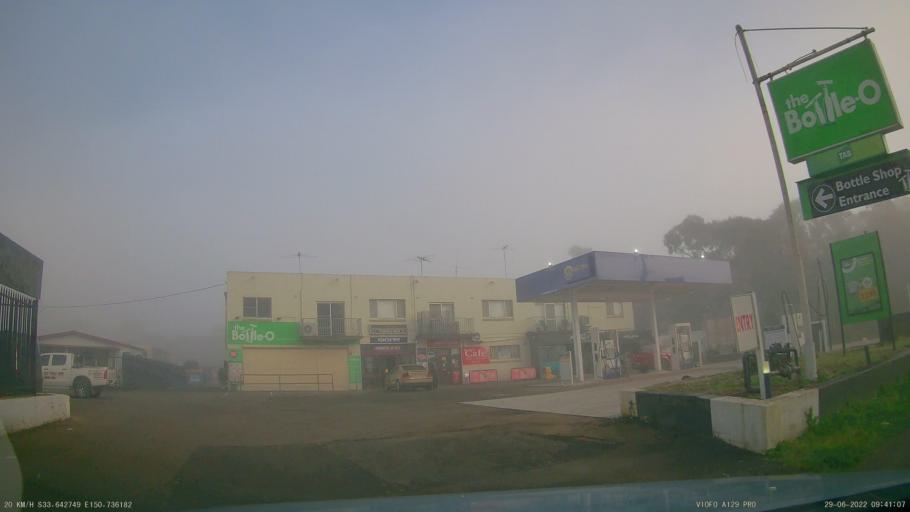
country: AU
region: New South Wales
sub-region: Hawkesbury
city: Richmond
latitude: -33.6427
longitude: 150.7361
